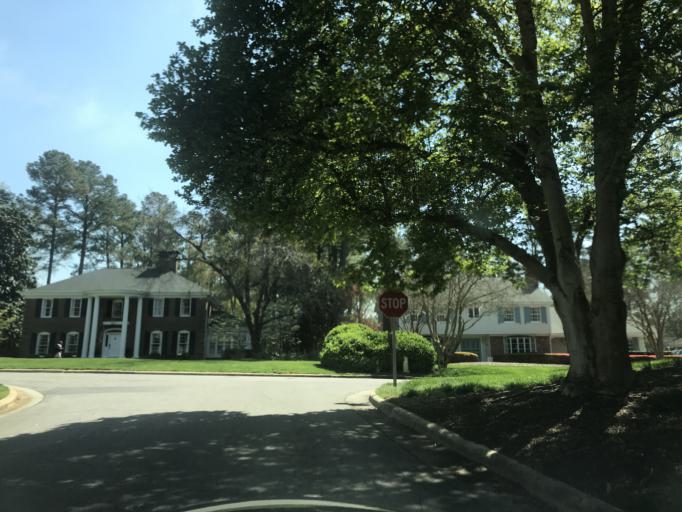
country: US
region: North Carolina
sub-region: Wake County
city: West Raleigh
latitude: 35.8306
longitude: -78.6427
